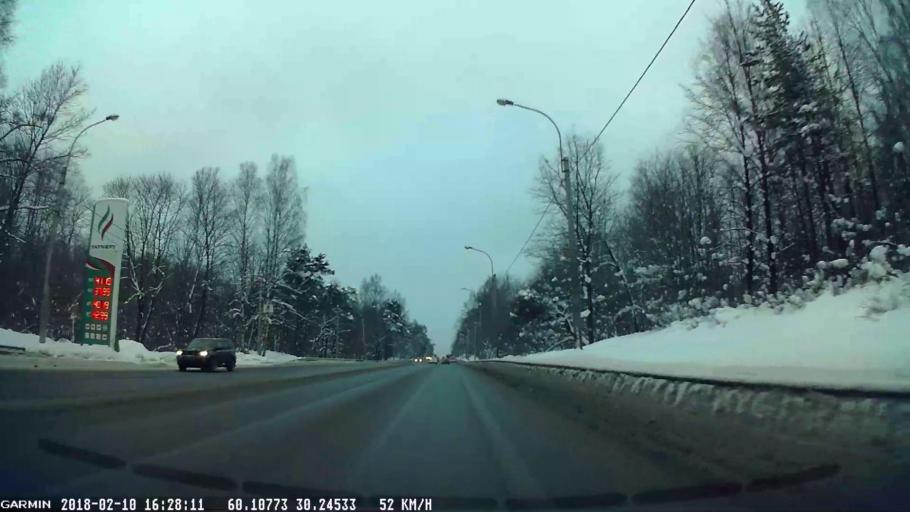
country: RU
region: St.-Petersburg
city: Levashovo
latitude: 60.1080
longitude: 30.2451
